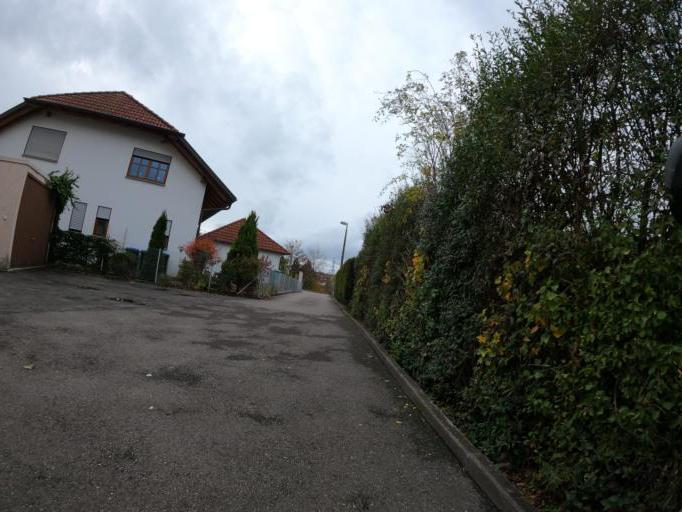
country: DE
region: Baden-Wuerttemberg
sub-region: Regierungsbezirk Stuttgart
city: Ehningen
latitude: 48.6927
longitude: 8.9393
